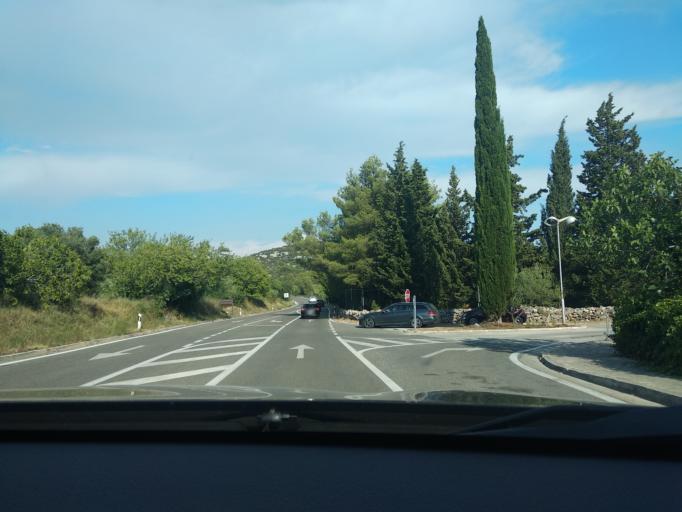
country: HR
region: Sibensko-Kniniska
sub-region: Grad Sibenik
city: Tisno
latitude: 43.8018
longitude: 15.6551
